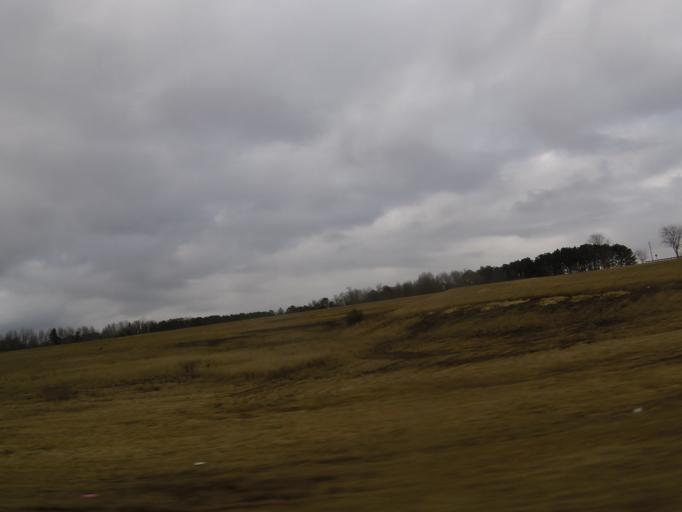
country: US
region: North Carolina
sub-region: Pitt County
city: Greenville
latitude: 35.6584
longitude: -77.3669
